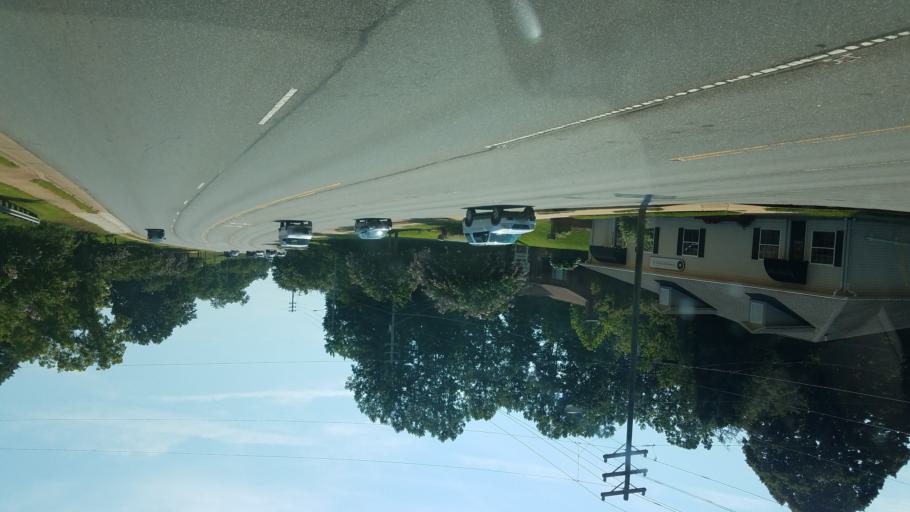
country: US
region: North Carolina
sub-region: Burke County
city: Morganton
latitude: 35.7370
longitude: -81.6775
